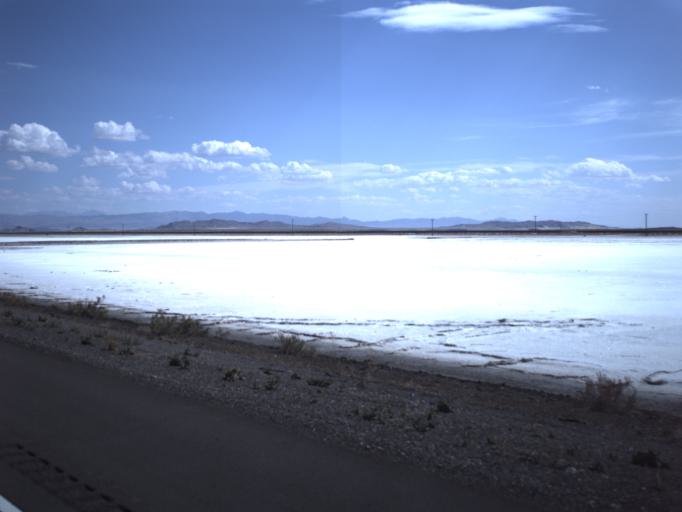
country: US
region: Utah
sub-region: Tooele County
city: Wendover
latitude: 40.7287
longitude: -113.4067
